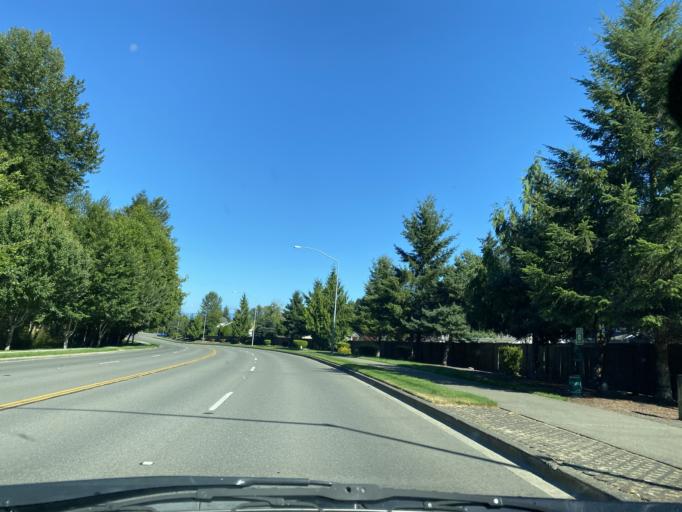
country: US
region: Washington
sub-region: Pierce County
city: South Hill
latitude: 47.1127
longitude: -122.2600
